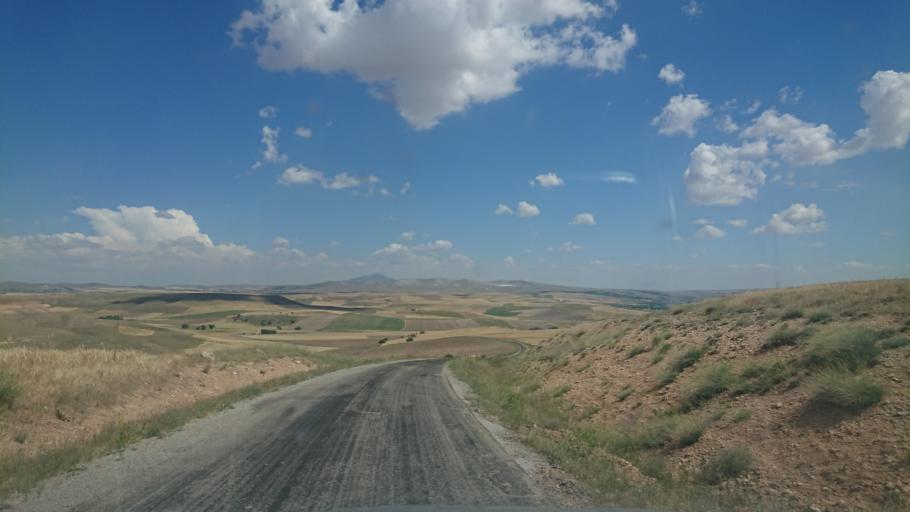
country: TR
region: Aksaray
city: Agacoren
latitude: 38.8053
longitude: 33.8102
